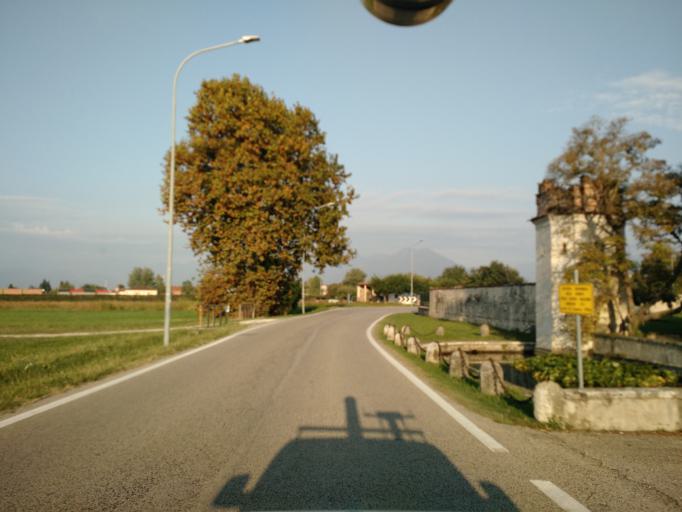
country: IT
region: Veneto
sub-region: Provincia di Vicenza
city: Sarcedo
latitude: 45.6982
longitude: 11.5383
